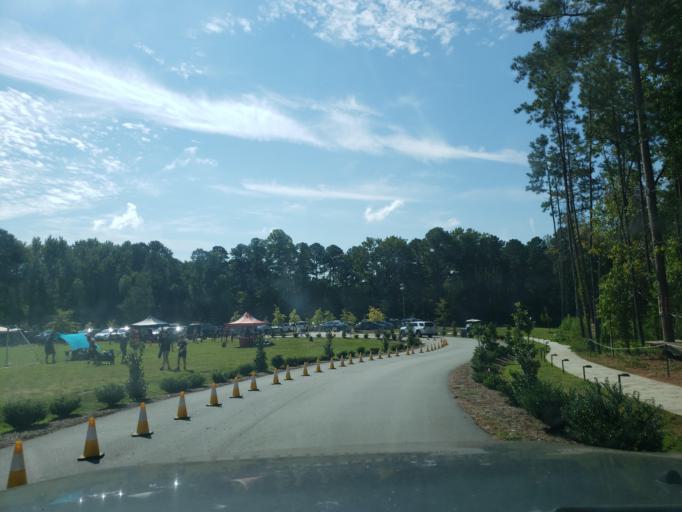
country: US
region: North Carolina
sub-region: Wake County
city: West Raleigh
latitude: 35.9385
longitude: -78.6968
